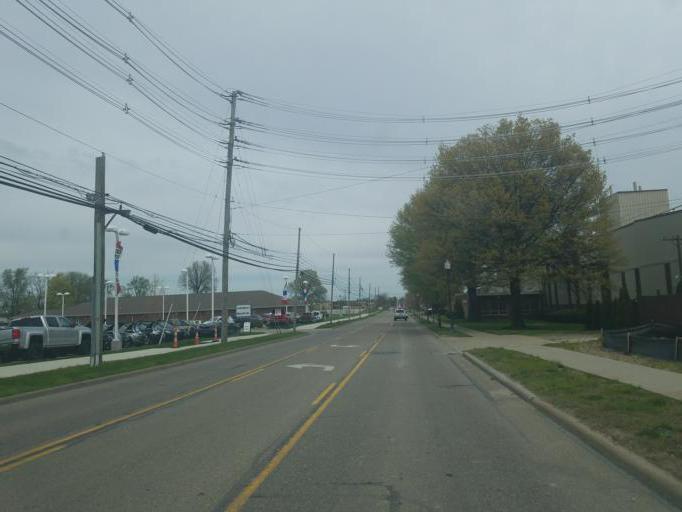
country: US
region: Ohio
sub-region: Wayne County
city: Orrville
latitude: 40.8509
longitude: -81.7639
